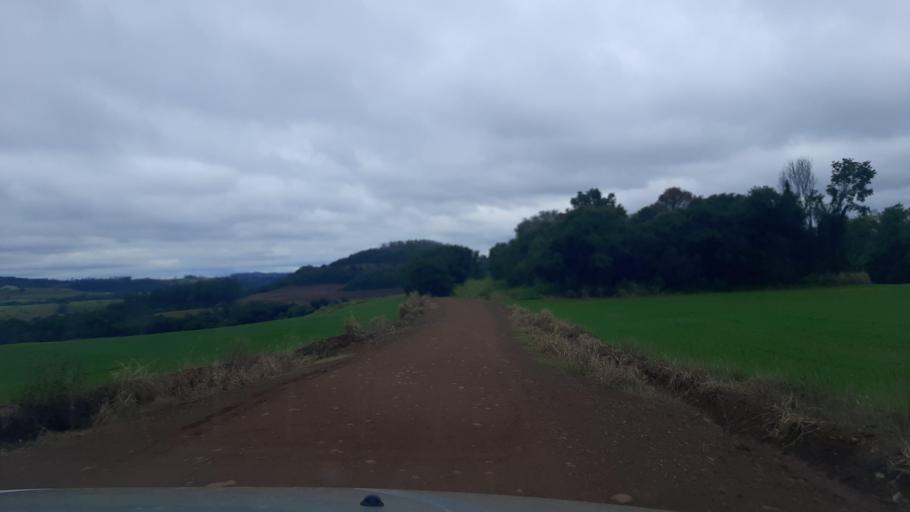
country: BR
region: Parana
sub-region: Ampere
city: Ampere
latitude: -26.0485
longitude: -53.5540
